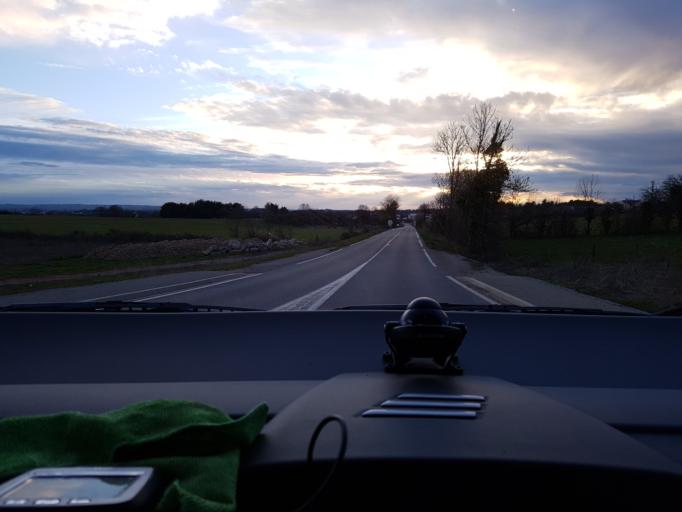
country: FR
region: Midi-Pyrenees
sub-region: Departement de l'Aveyron
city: Sebazac-Concoures
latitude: 44.4005
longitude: 2.6185
